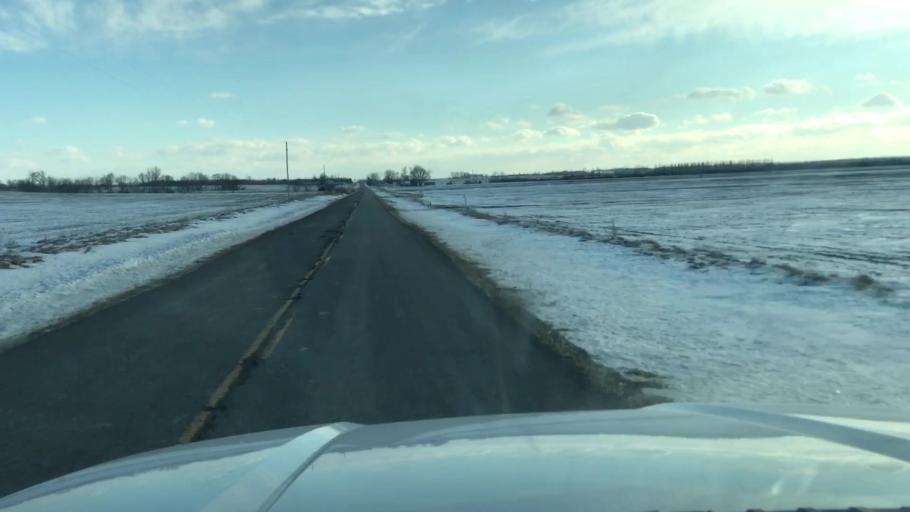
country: US
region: Missouri
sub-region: Holt County
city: Oregon
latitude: 40.1258
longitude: -95.0225
